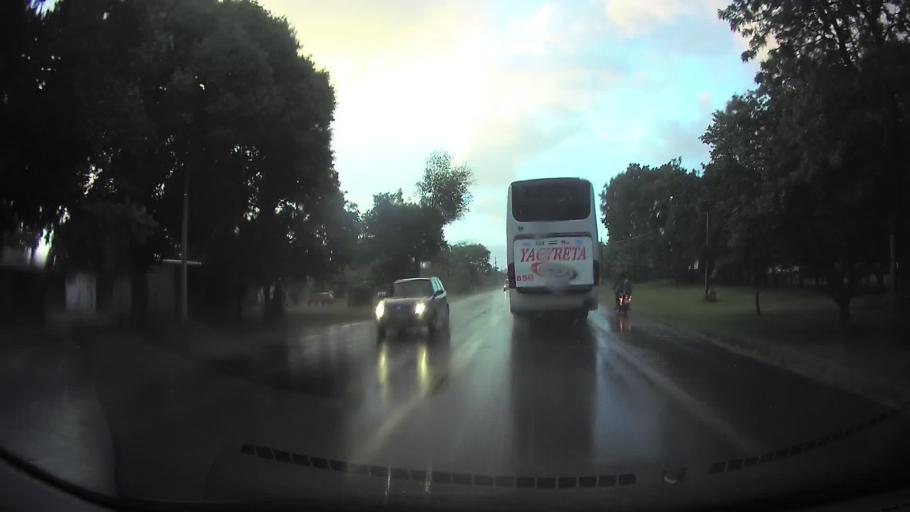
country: PY
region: Paraguari
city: Yaguaron
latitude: -25.5852
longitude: -57.2422
